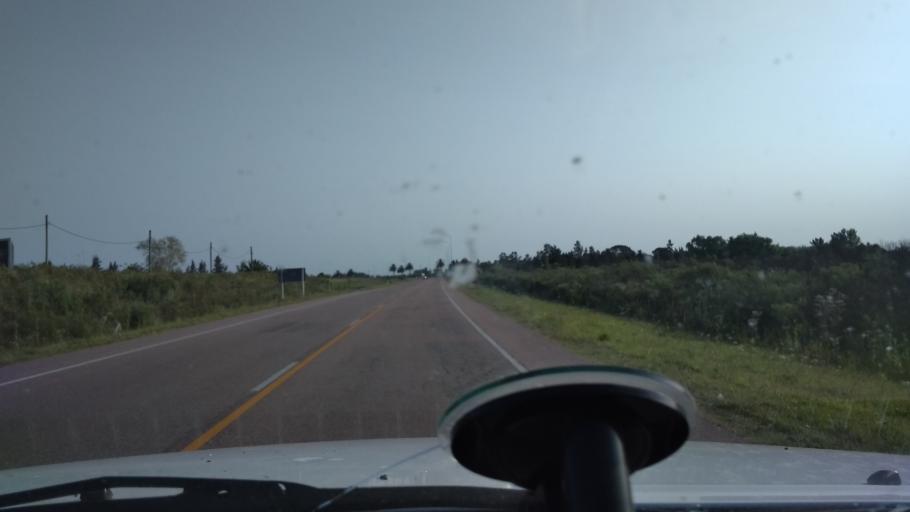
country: UY
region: Canelones
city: Sauce
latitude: -34.6599
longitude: -56.0562
